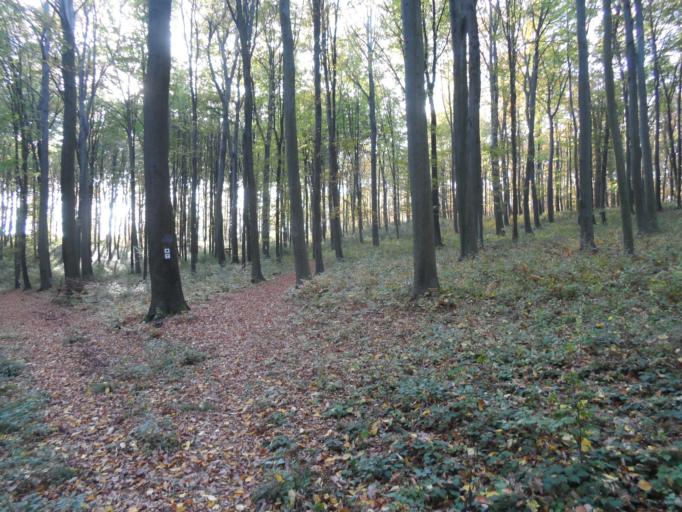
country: HU
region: Veszprem
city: Urkut
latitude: 47.1921
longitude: 17.6453
